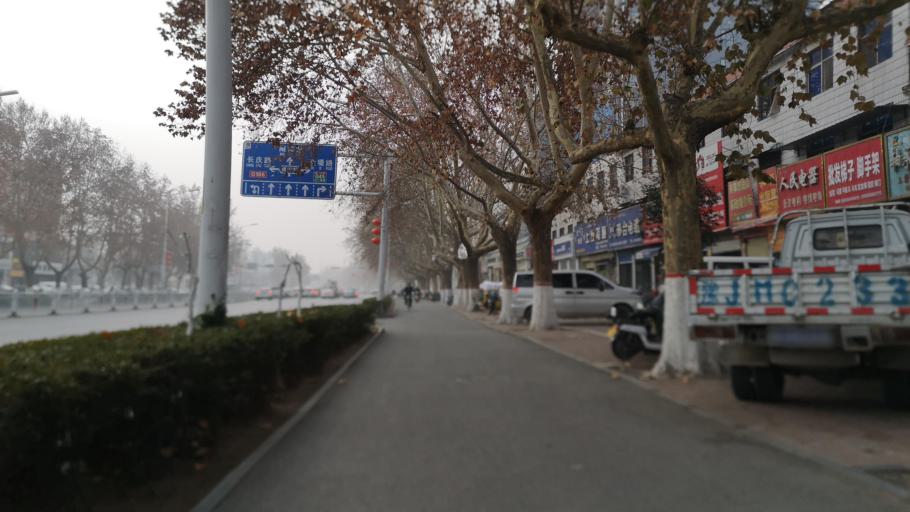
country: CN
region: Henan Sheng
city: Zhongyuanlu
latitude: 35.7736
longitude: 115.0397
